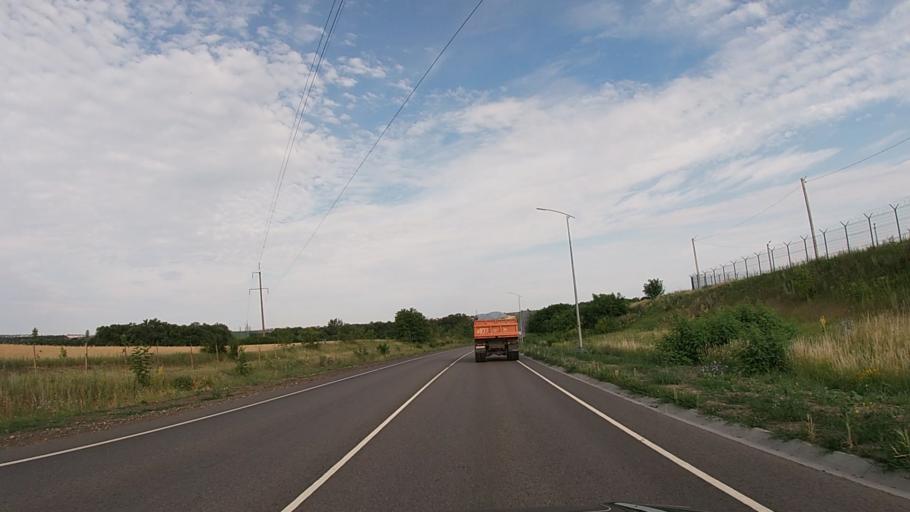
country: RU
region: Belgorod
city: Severnyy
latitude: 50.6663
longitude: 36.4963
